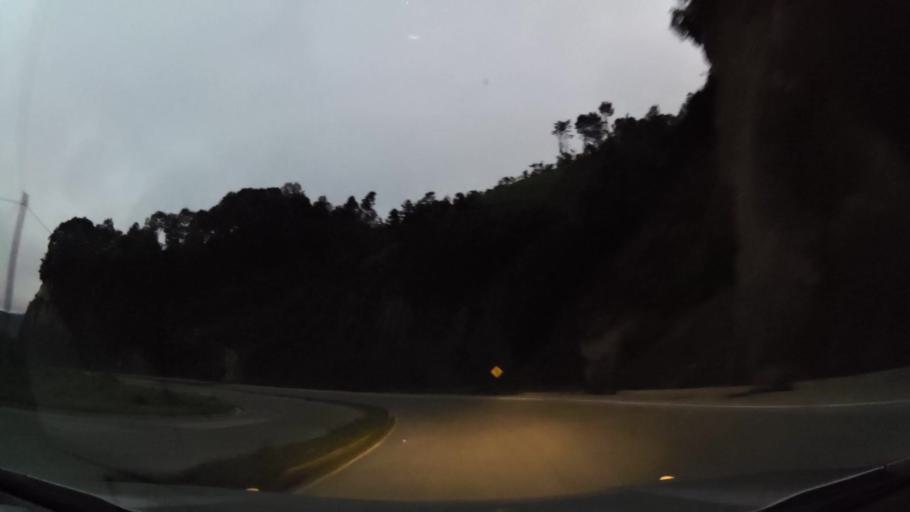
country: GT
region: Chimaltenango
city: Santa Apolonia
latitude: 14.8185
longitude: -91.0038
